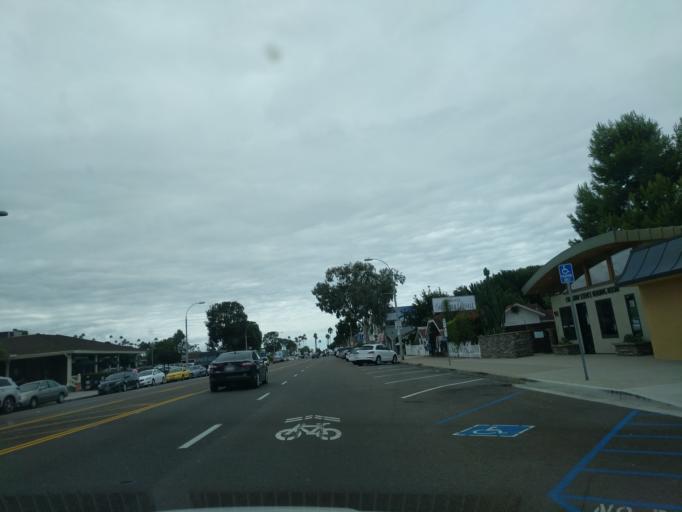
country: US
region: California
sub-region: San Diego County
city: Encinitas
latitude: 33.0406
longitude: -117.2932
